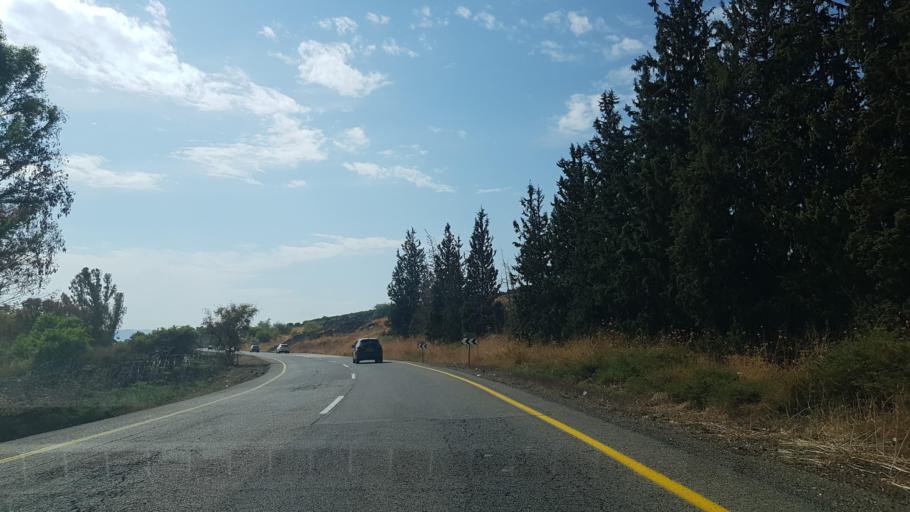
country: SY
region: Quneitra
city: Al Butayhah
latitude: 32.8967
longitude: 35.6049
